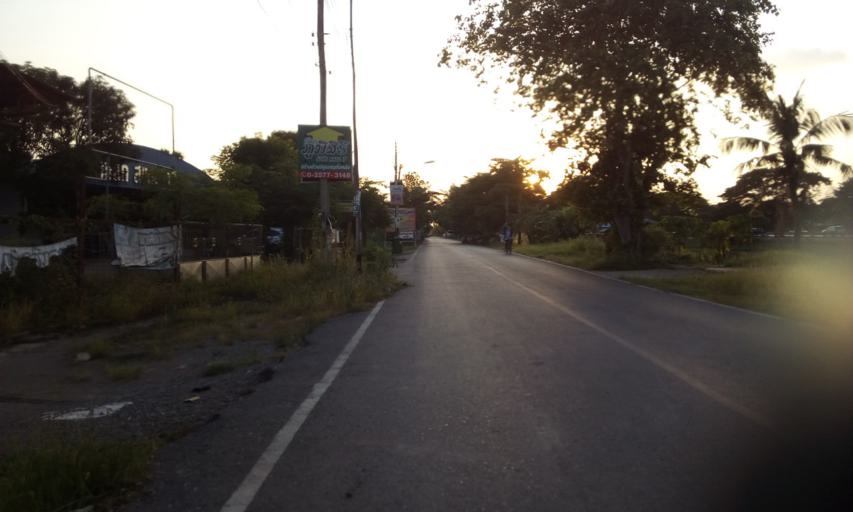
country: TH
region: Pathum Thani
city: Ban Rangsit
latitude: 14.0391
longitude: 100.7868
